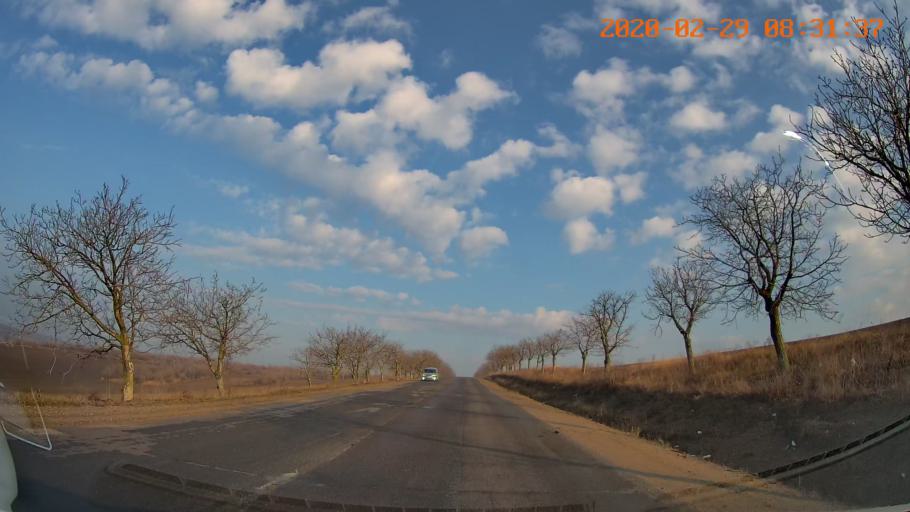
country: MD
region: Anenii Noi
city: Anenii Noi
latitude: 46.9152
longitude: 29.2890
